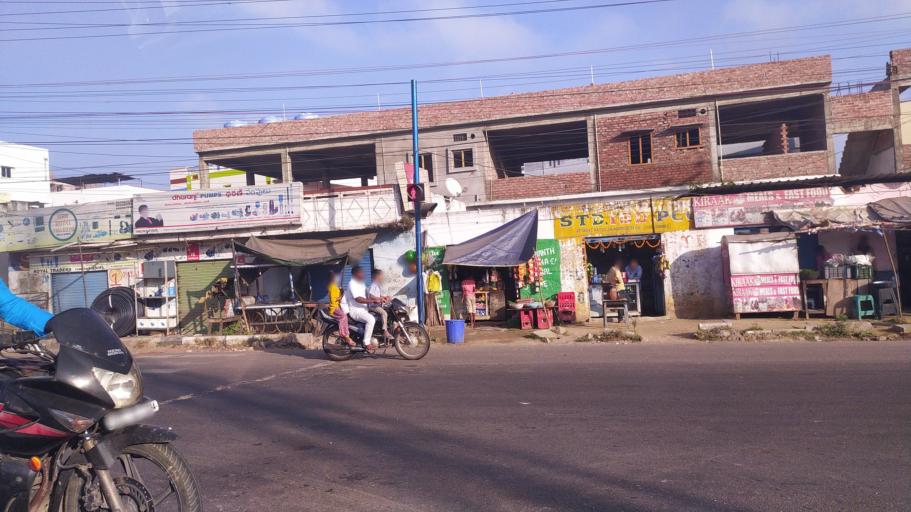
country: IN
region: Telangana
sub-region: Rangareddi
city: Balapur
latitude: 17.3160
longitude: 78.4488
